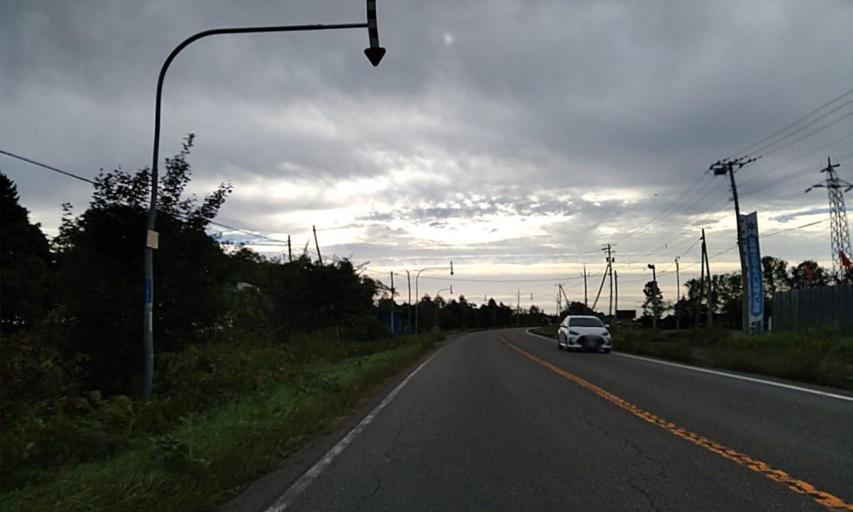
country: JP
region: Hokkaido
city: Obihiro
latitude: 42.9332
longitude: 142.9743
